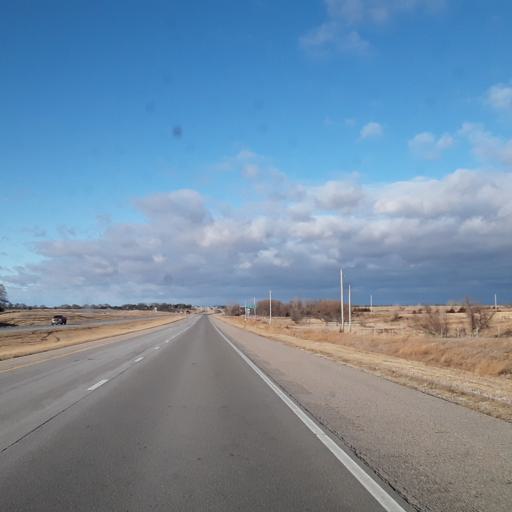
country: US
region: Kansas
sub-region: Republic County
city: Belleville
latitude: 39.9384
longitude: -97.6141
